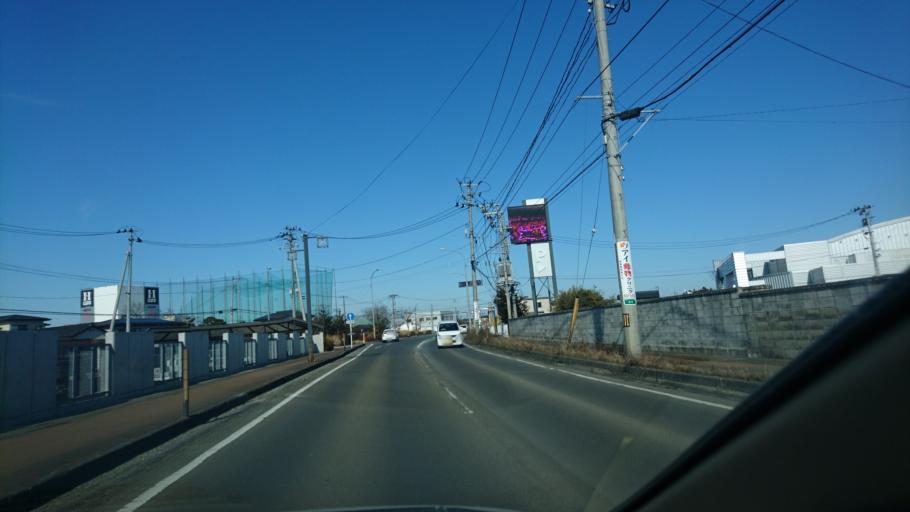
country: JP
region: Miyagi
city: Furukawa
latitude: 38.5969
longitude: 140.9765
